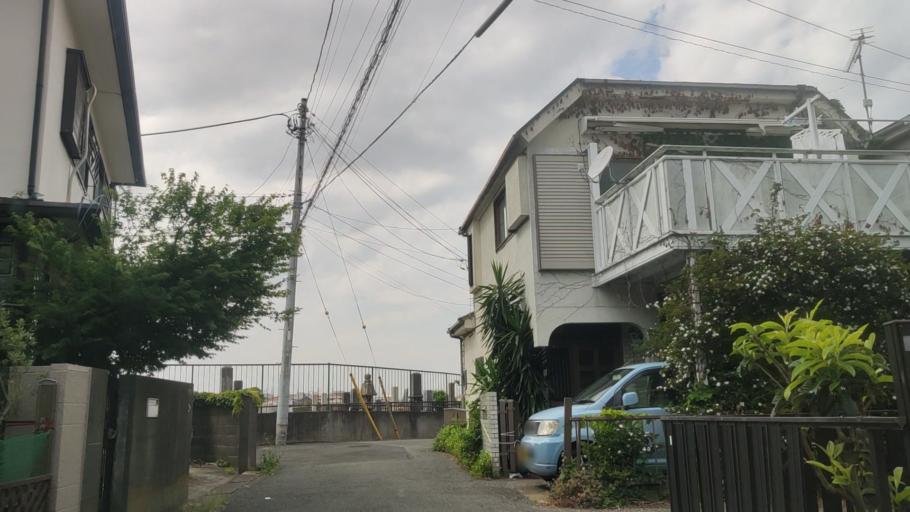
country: JP
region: Kanagawa
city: Yokohama
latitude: 35.4270
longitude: 139.6346
